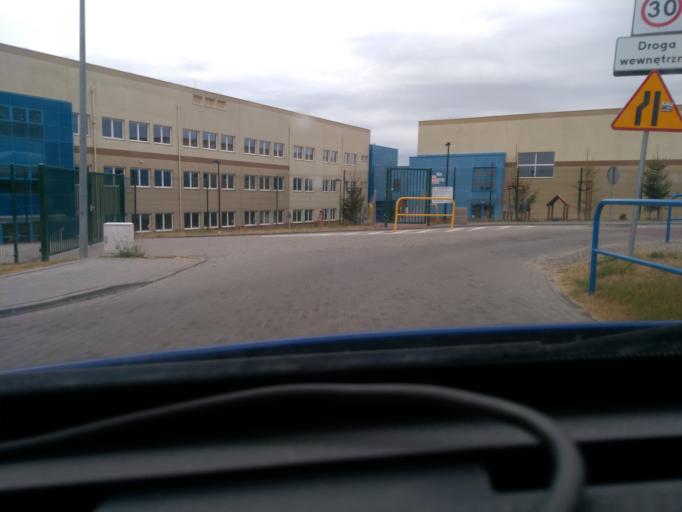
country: PL
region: Pomeranian Voivodeship
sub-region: Powiat kartuski
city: Banino
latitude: 54.3960
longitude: 18.3988
